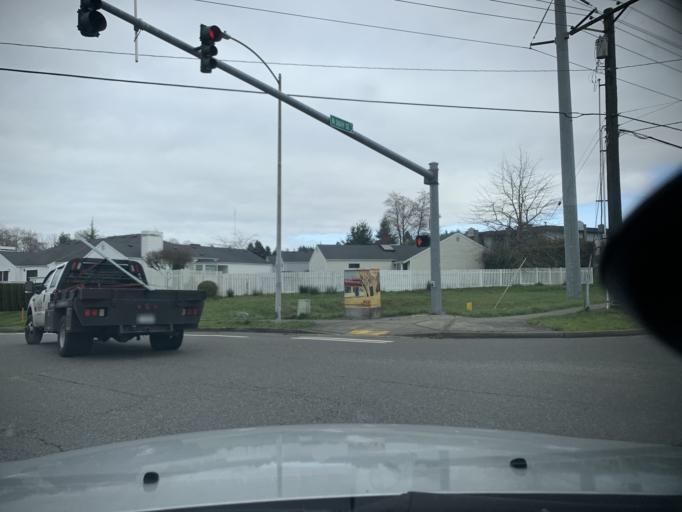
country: US
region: Washington
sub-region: Pierce County
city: Fircrest
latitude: 47.2721
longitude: -122.5239
